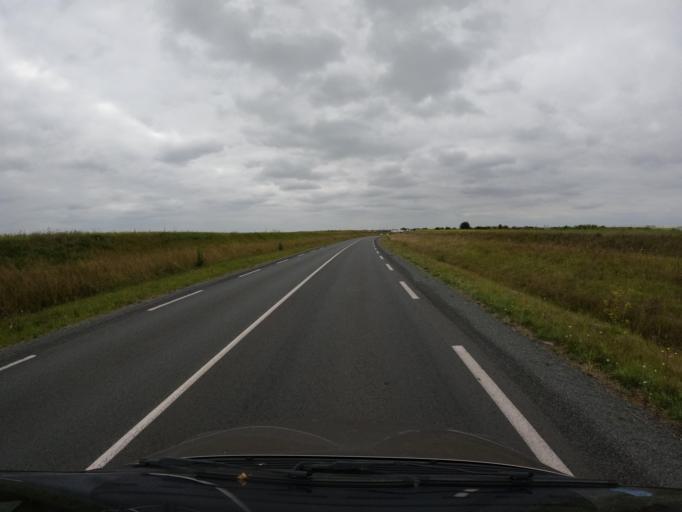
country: FR
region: Pays de la Loire
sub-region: Departement de la Vendee
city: Fontenay-le-Comte
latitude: 46.4430
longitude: -0.7996
